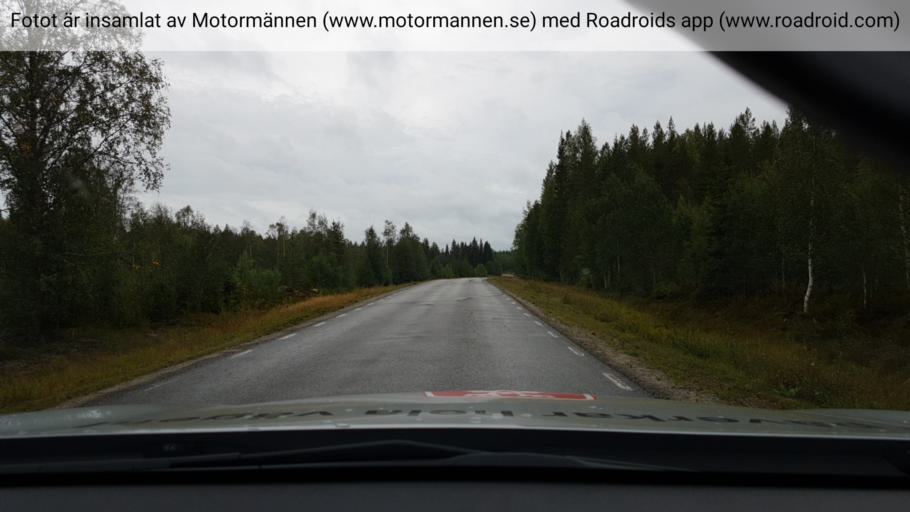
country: SE
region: Vaesterbotten
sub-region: Skelleftea Kommun
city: Burtraesk
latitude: 64.3002
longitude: 20.6483
